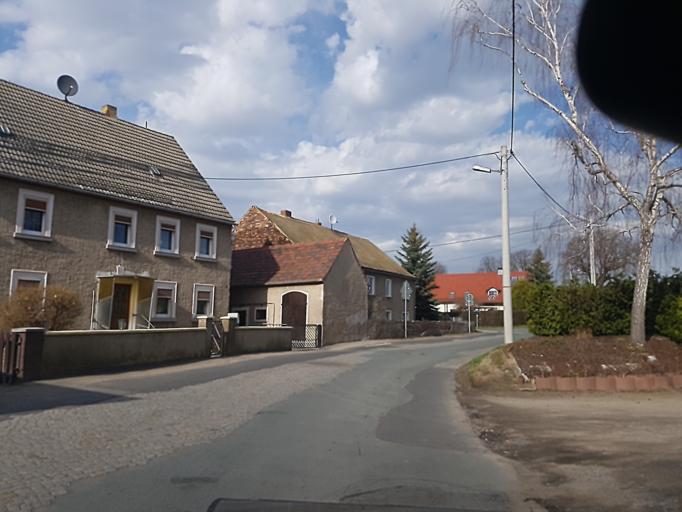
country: DE
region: Saxony
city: Stauchitz
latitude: 51.3044
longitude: 13.1809
